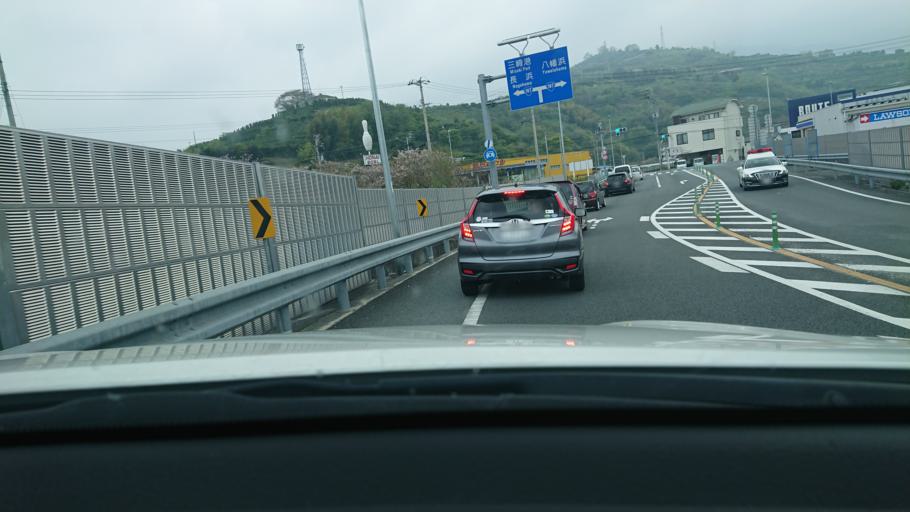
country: JP
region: Ehime
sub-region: Nishiuwa-gun
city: Ikata-cho
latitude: 33.4827
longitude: 132.4048
